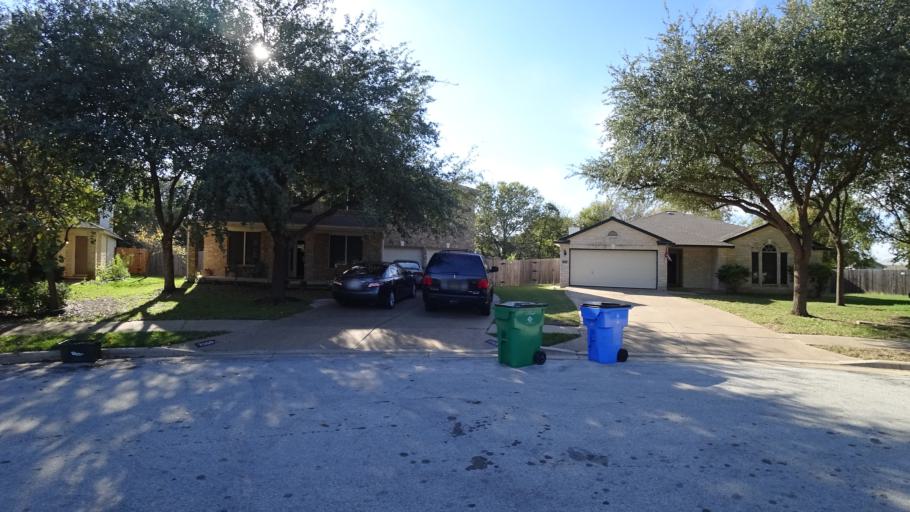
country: US
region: Texas
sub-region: Travis County
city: Wells Branch
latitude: 30.4609
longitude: -97.6885
